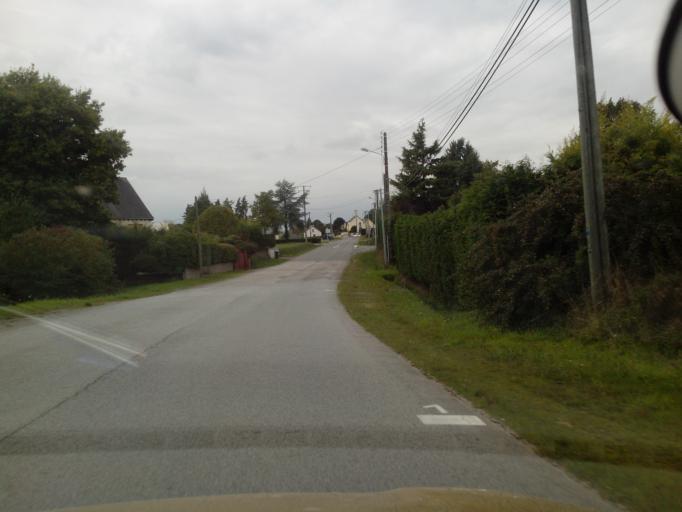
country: FR
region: Brittany
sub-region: Departement du Morbihan
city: Mauron
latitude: 48.0772
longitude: -2.2953
